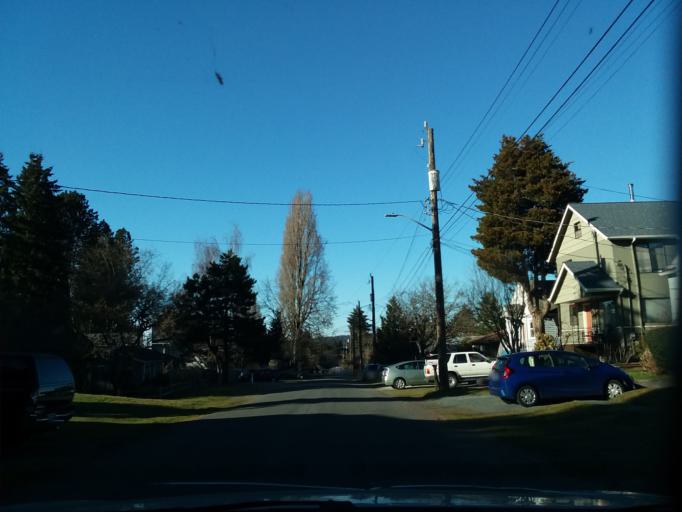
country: US
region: Washington
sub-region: King County
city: Shoreline
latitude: 47.6947
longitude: -122.3673
